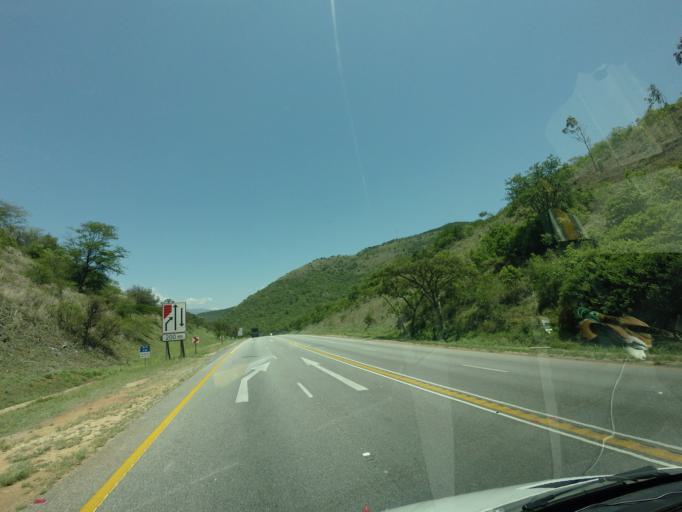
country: ZA
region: Mpumalanga
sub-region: Ehlanzeni District
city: Nelspruit
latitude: -25.4450
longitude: 30.7196
